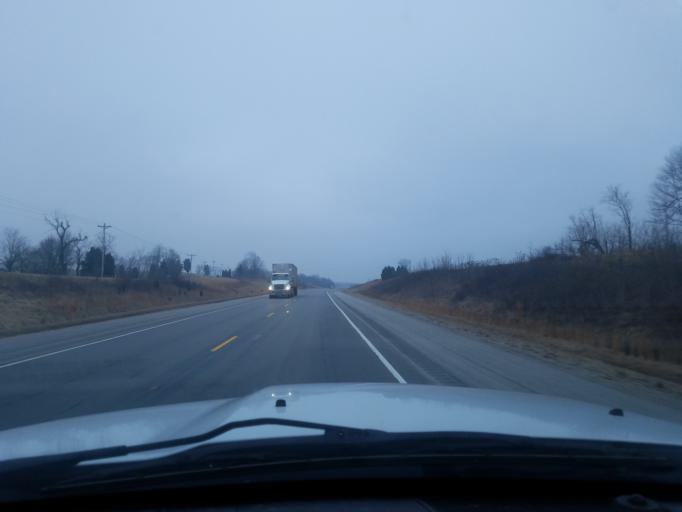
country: US
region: Indiana
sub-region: Perry County
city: Tell City
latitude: 38.1288
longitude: -86.6054
